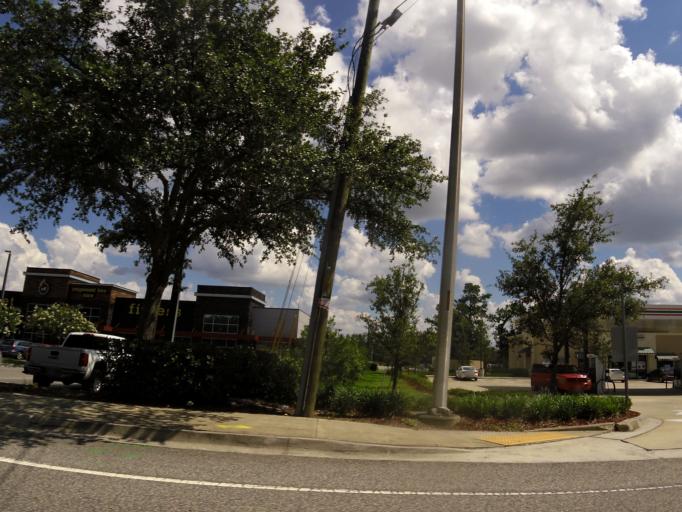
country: US
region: Florida
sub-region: Saint Johns County
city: Fruit Cove
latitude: 30.1404
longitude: -81.5233
